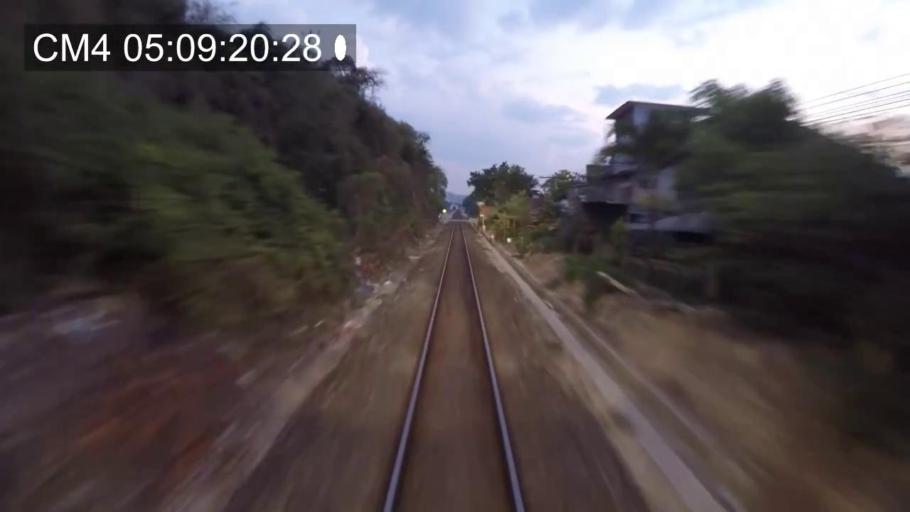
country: VN
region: Khanh Hoa
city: Nha Trang
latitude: 12.2999
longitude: 109.1858
